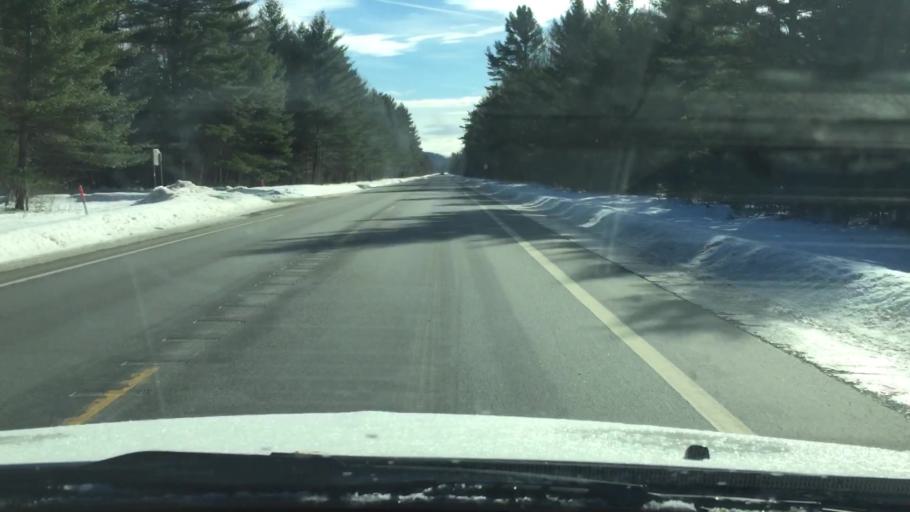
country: US
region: Michigan
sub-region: Antrim County
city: Mancelona
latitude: 45.0340
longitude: -85.0673
